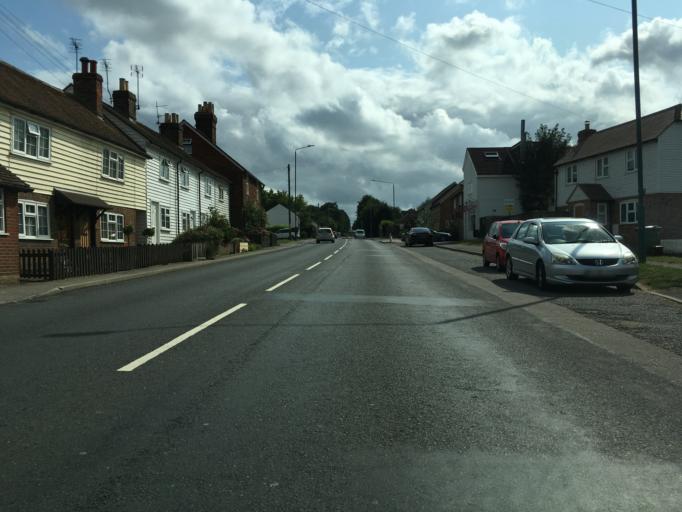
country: GB
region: England
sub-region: Kent
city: Maidstone
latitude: 51.2335
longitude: 0.5149
